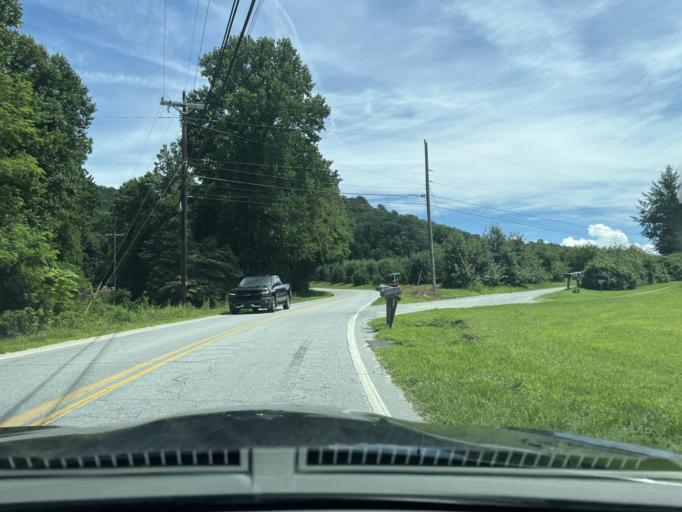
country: US
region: North Carolina
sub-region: Henderson County
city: Edneyville
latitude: 35.3878
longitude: -82.3273
